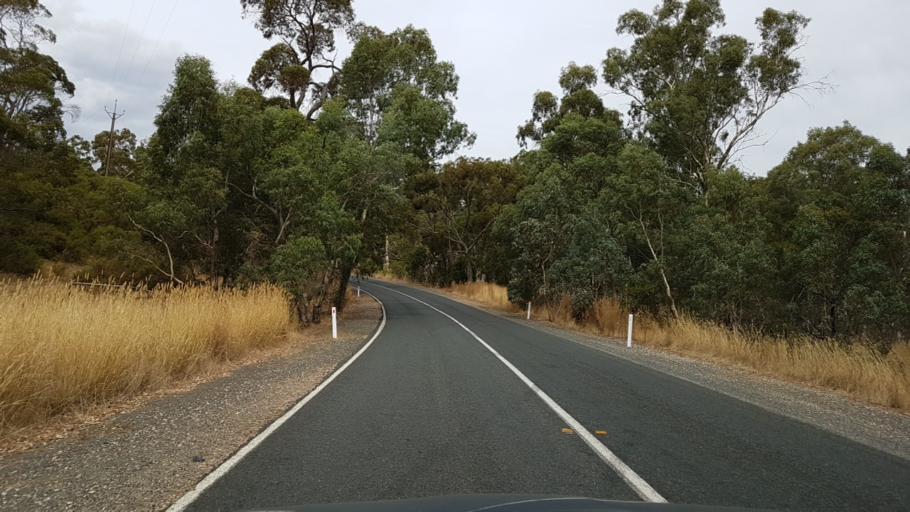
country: AU
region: South Australia
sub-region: Adelaide Hills
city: Birdwood
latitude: -34.7896
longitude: 138.9461
